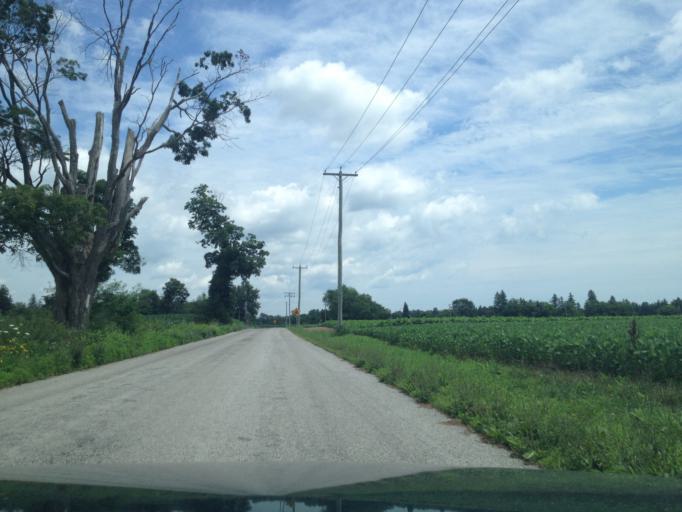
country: CA
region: Ontario
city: Norfolk County
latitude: 42.7824
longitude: -80.2878
